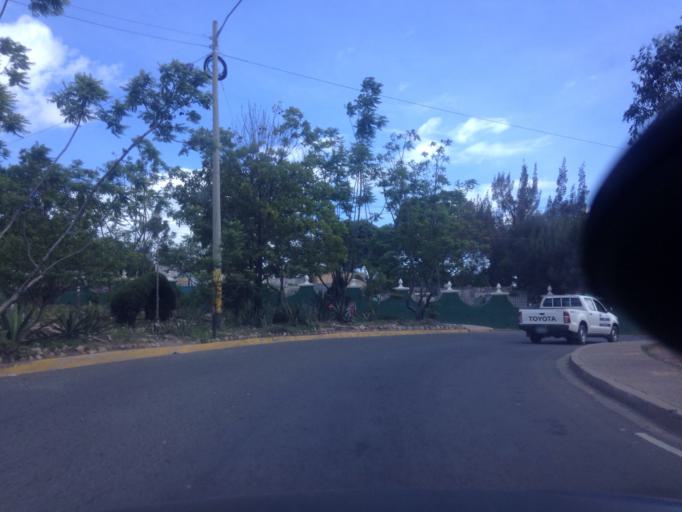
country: HN
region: Francisco Morazan
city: Santa Lucia
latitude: 14.0821
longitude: -87.1586
